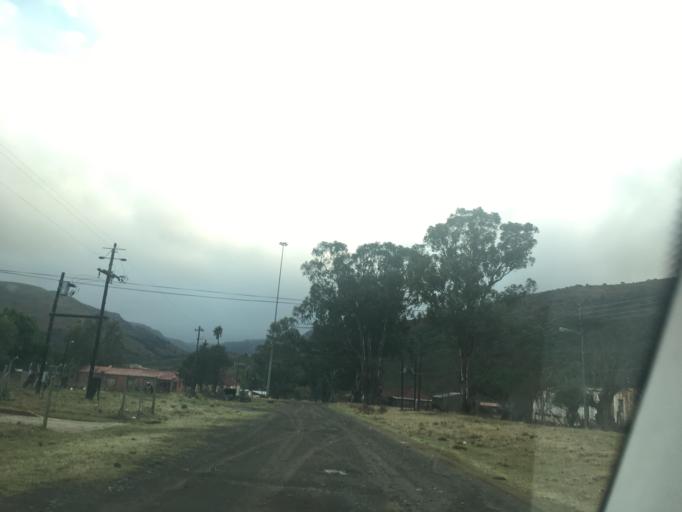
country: ZA
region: Eastern Cape
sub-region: Chris Hani District Municipality
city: Cala
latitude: -31.5229
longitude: 27.6995
